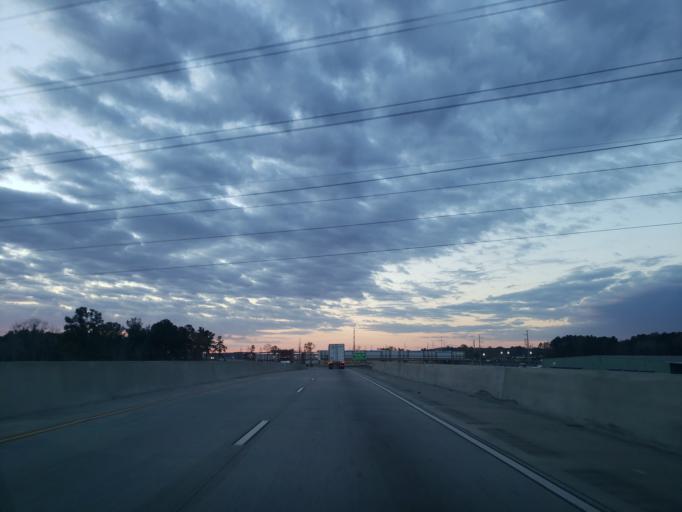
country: US
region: Georgia
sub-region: Chatham County
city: Port Wentworth
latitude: 32.1533
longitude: -81.1760
